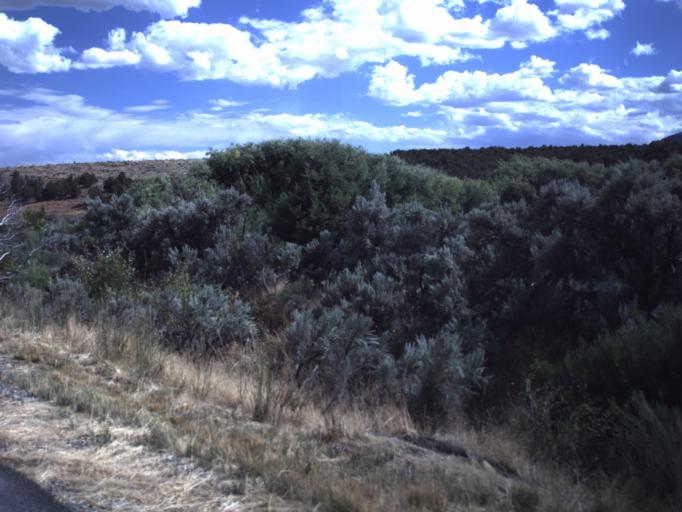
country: US
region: Utah
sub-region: Tooele County
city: Grantsville
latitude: 40.3338
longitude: -112.5235
